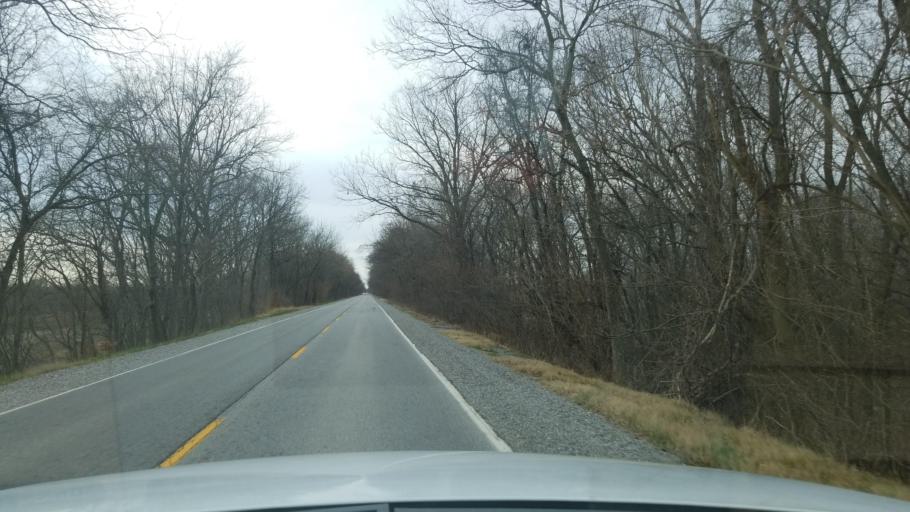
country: US
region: Illinois
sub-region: White County
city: Carmi
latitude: 37.9286
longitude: -88.0952
